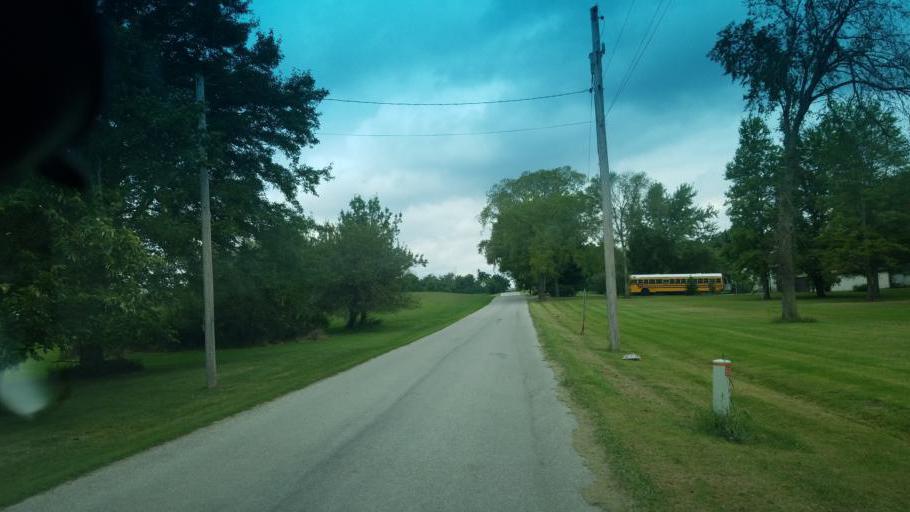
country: US
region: Ohio
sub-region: Richland County
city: Ontario
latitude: 40.8168
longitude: -82.5614
